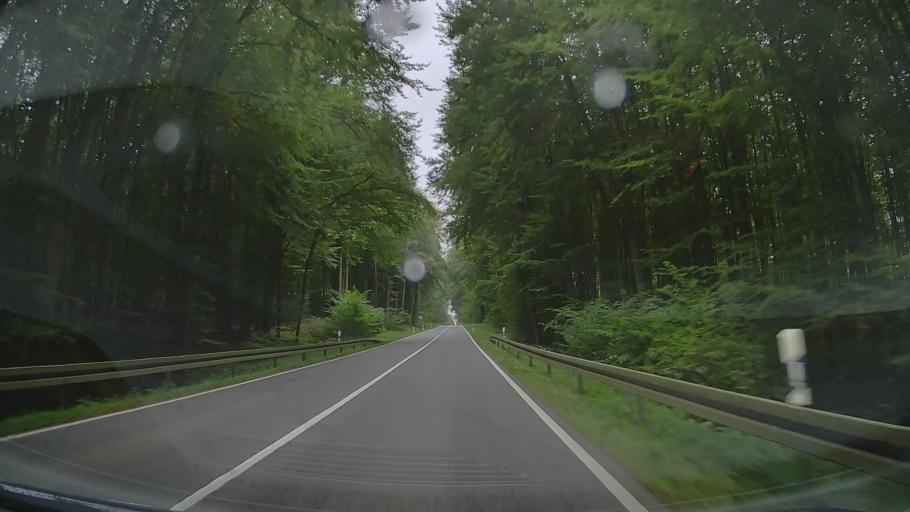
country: DE
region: Mecklenburg-Vorpommern
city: Tarnow
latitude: 53.7354
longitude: 11.9944
